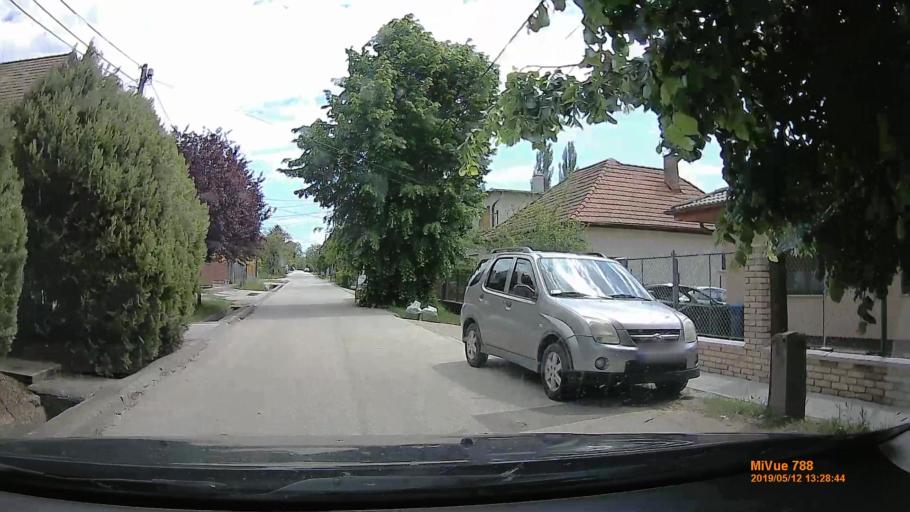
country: HU
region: Budapest
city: Budapest XVII. keruelet
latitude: 47.4801
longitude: 19.2953
